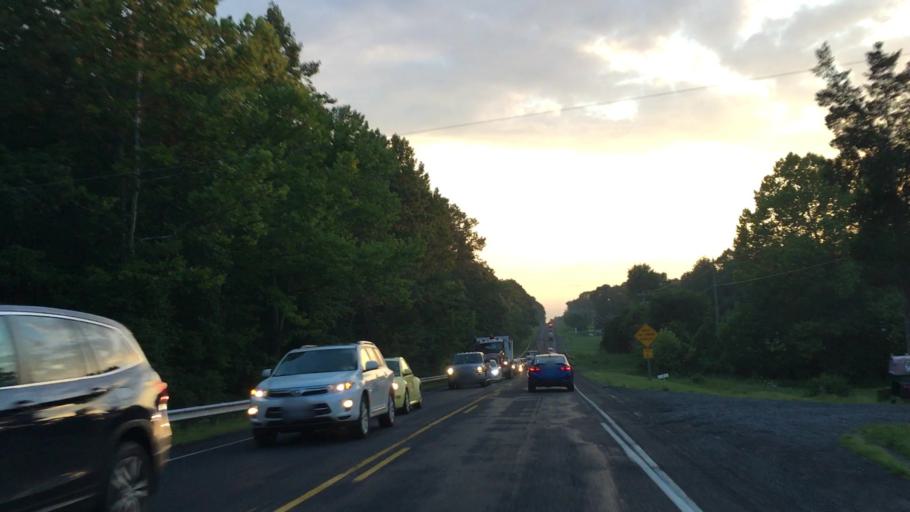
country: US
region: Virginia
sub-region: Spotsylvania County
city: Spotsylvania
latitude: 38.3091
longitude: -77.7918
